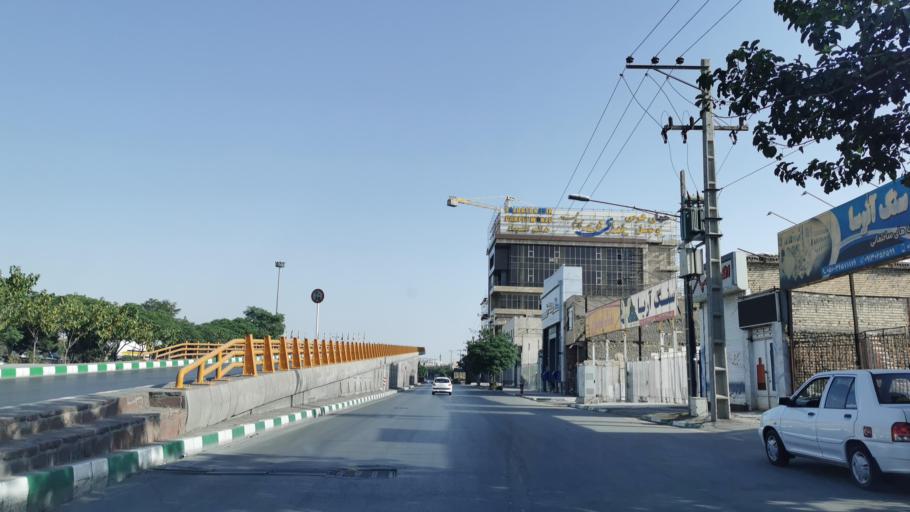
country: IR
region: Razavi Khorasan
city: Mashhad
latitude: 36.3681
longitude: 59.5355
